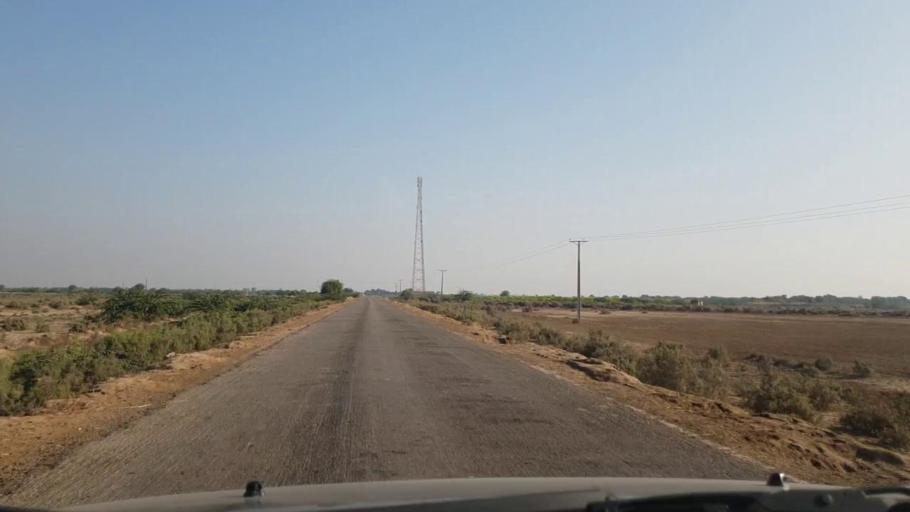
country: PK
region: Sindh
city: Tando Bago
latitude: 24.8537
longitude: 69.0396
